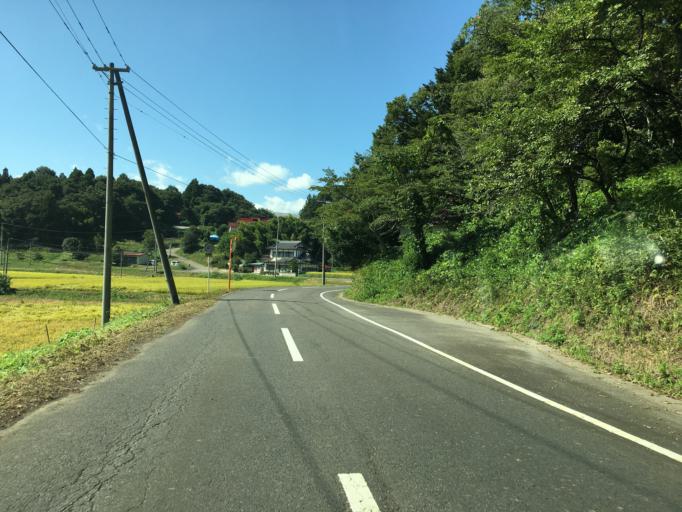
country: JP
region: Fukushima
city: Sukagawa
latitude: 37.2834
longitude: 140.4369
